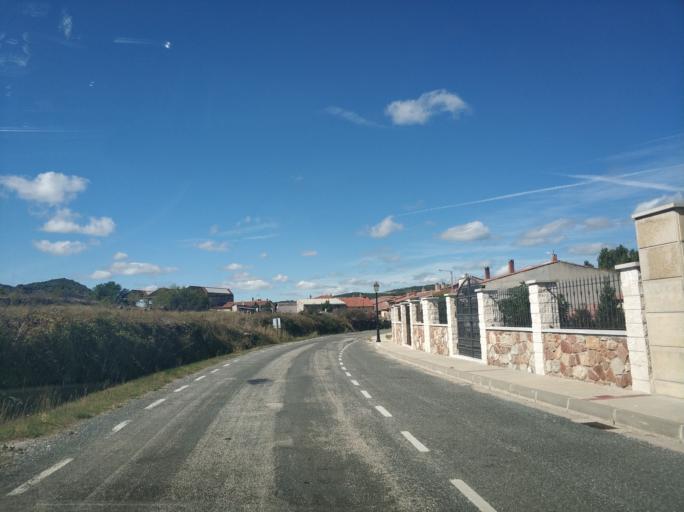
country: ES
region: Castille and Leon
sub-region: Provincia de Soria
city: Espejon
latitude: 41.8295
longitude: -3.2563
